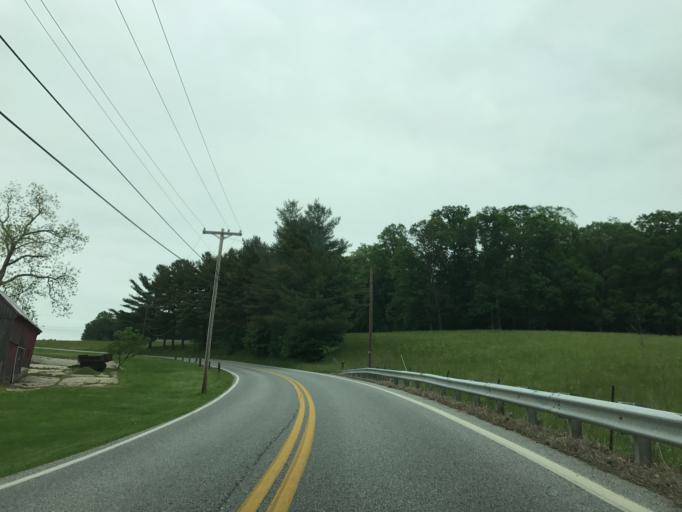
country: US
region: Pennsylvania
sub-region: York County
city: New Freedom
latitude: 39.7096
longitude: -76.6738
